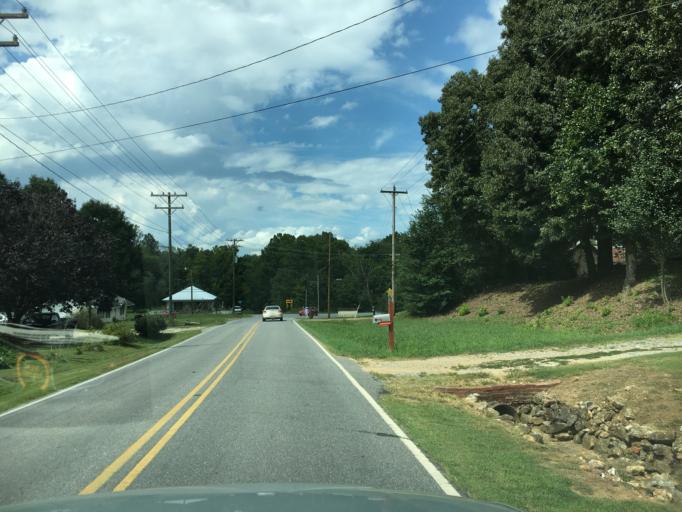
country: US
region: North Carolina
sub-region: Catawba County
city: Maiden
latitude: 35.5820
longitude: -81.1951
